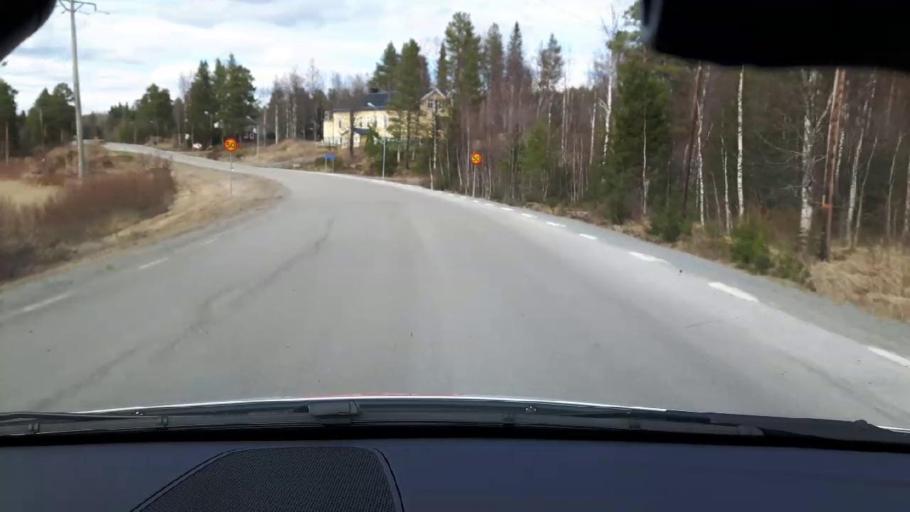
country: SE
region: Jaemtland
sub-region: Bergs Kommun
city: Hoverberg
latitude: 62.6595
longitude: 14.7455
